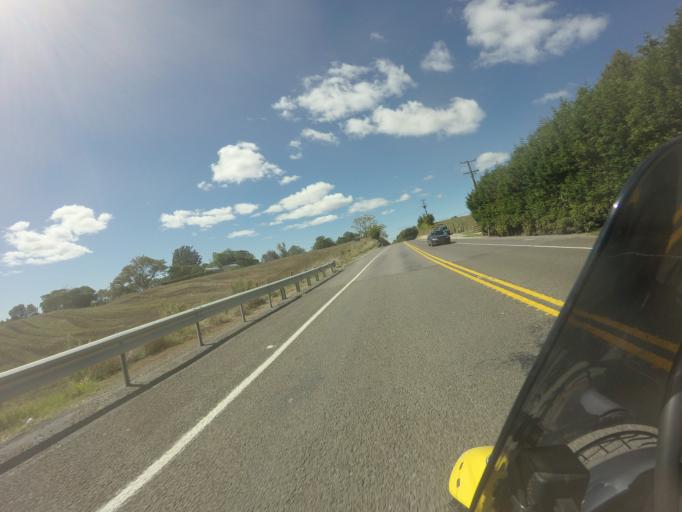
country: NZ
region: Bay of Plenty
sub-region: Whakatane District
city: Edgecumbe
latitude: -37.9983
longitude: 176.8737
